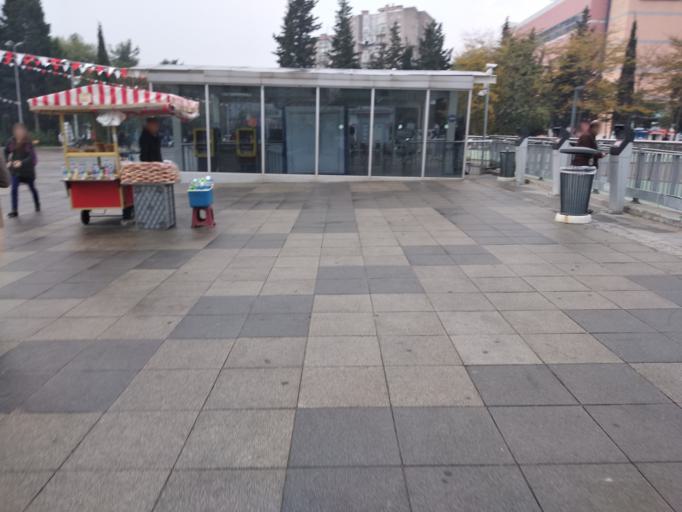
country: TR
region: Istanbul
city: Esenyurt
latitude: 41.0122
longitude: 28.6507
